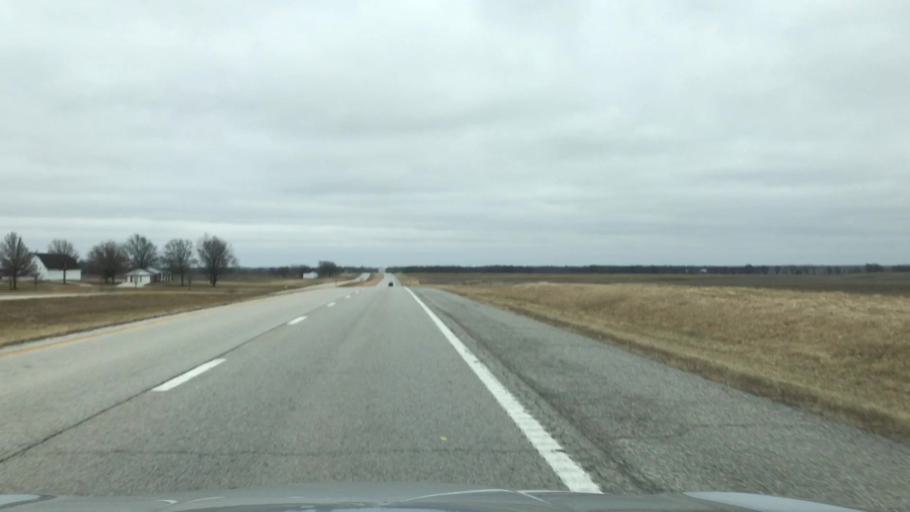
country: US
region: Missouri
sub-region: Livingston County
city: Chillicothe
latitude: 39.7764
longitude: -93.4733
